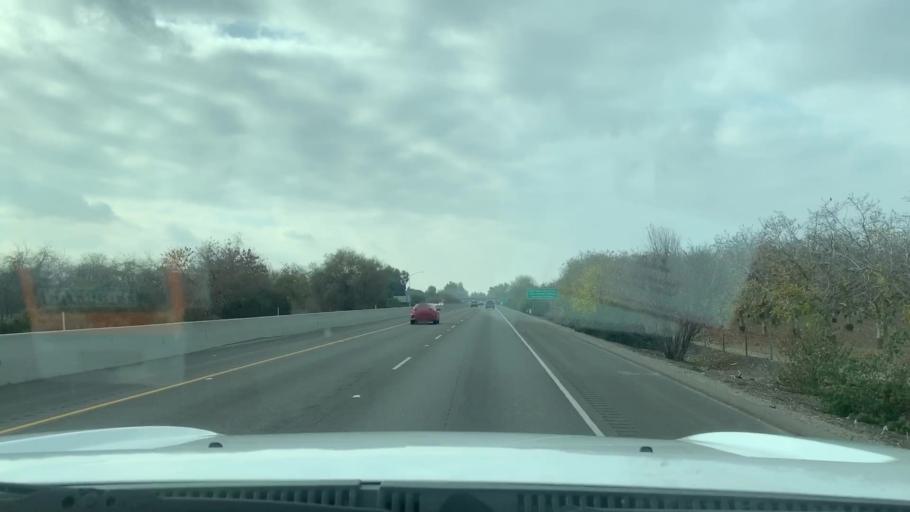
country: US
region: California
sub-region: Kings County
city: Lemoore
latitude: 36.2917
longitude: -119.7728
